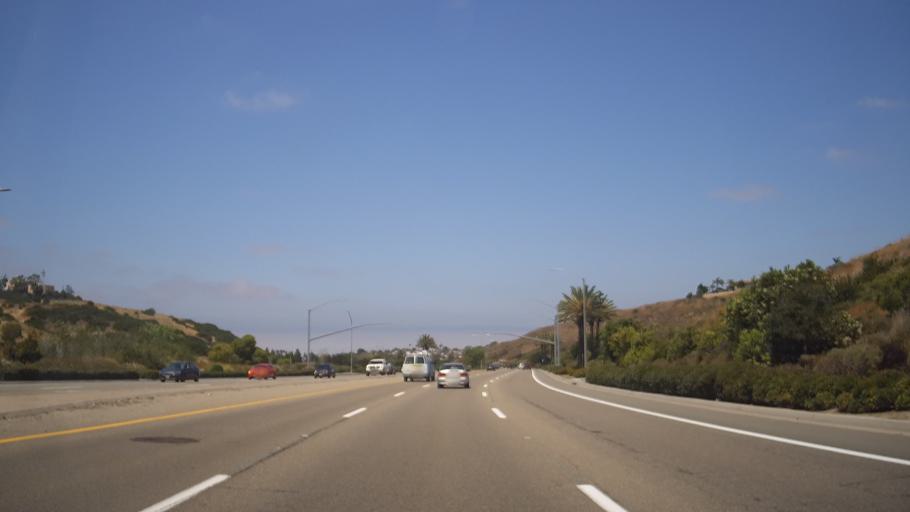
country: US
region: California
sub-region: San Diego County
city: Bonita
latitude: 32.6093
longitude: -117.0194
